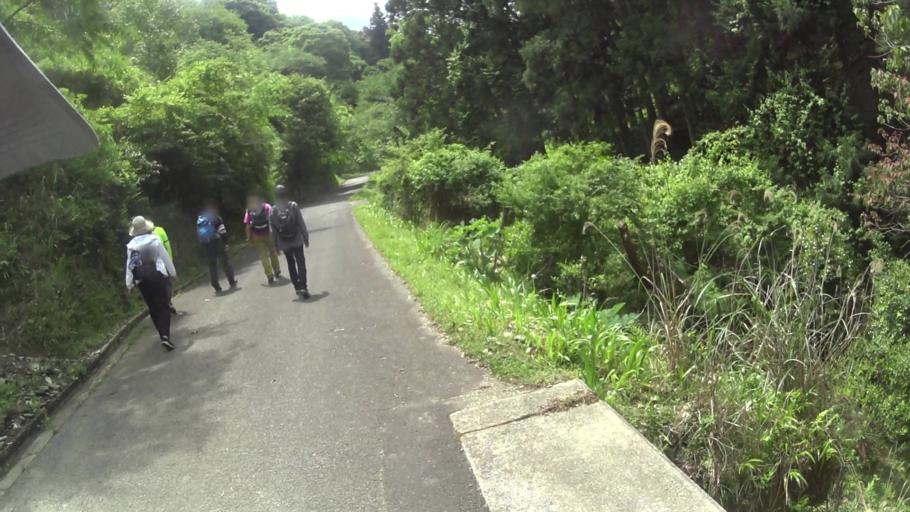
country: JP
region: Nara
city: Yoshino-cho
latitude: 34.3648
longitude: 135.8660
